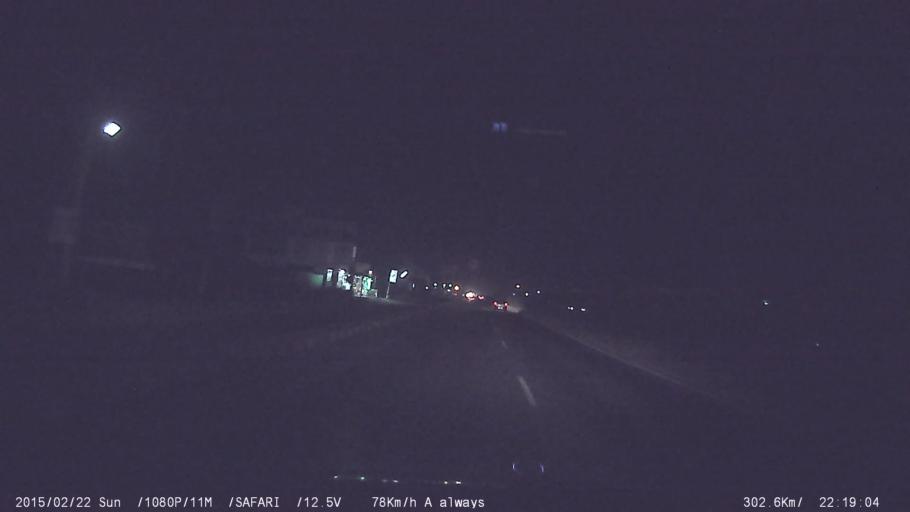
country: IN
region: Tamil Nadu
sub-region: Karur
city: Karur
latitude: 10.9762
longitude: 78.0632
